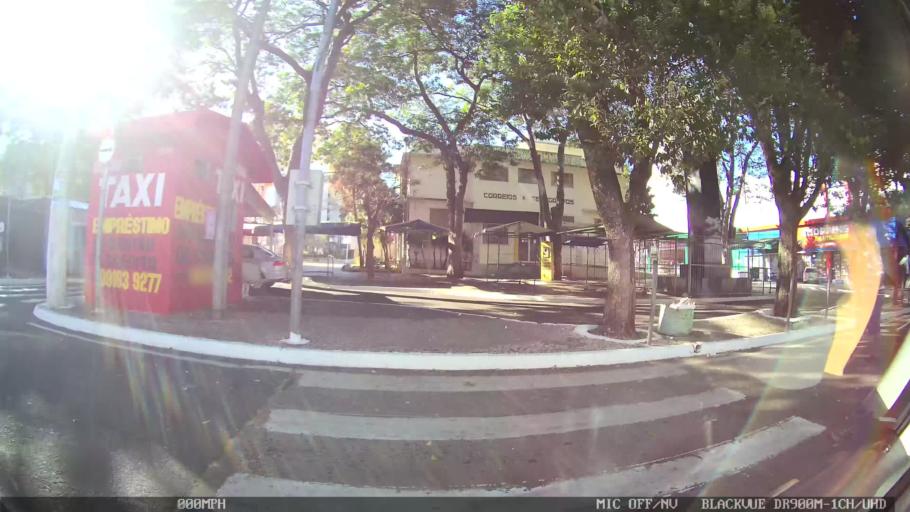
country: BR
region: Sao Paulo
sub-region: Franca
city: Franca
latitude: -20.5376
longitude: -47.4031
